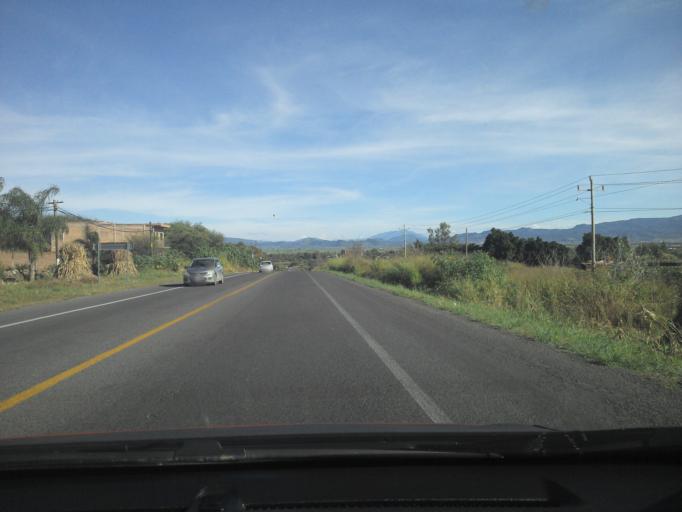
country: MX
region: Jalisco
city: Teuchitlan
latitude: 20.6784
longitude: -103.8383
